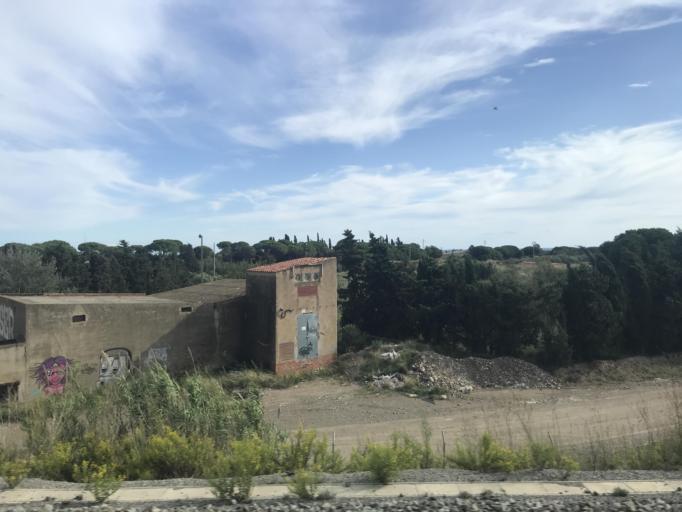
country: ES
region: Catalonia
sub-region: Provincia de Tarragona
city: Cambrils
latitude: 41.0920
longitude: 1.0788
